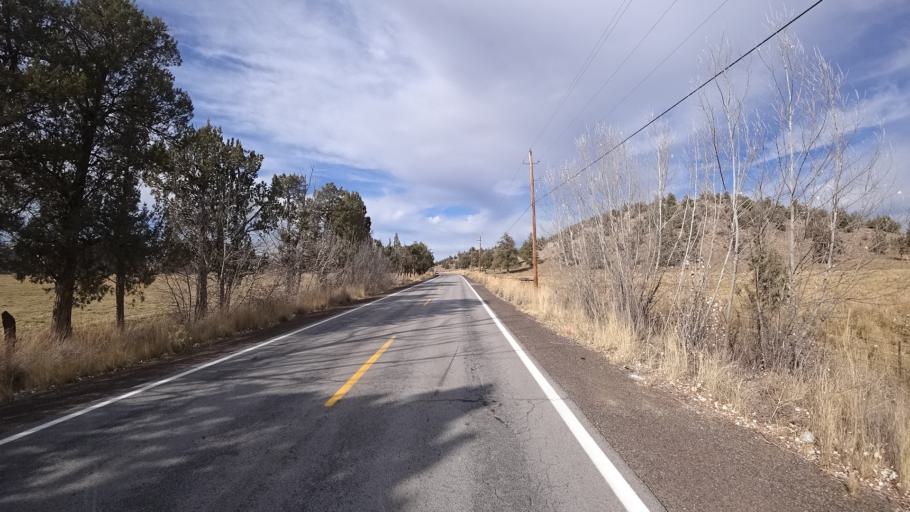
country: US
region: California
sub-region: Siskiyou County
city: Weed
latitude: 41.5704
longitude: -122.3896
